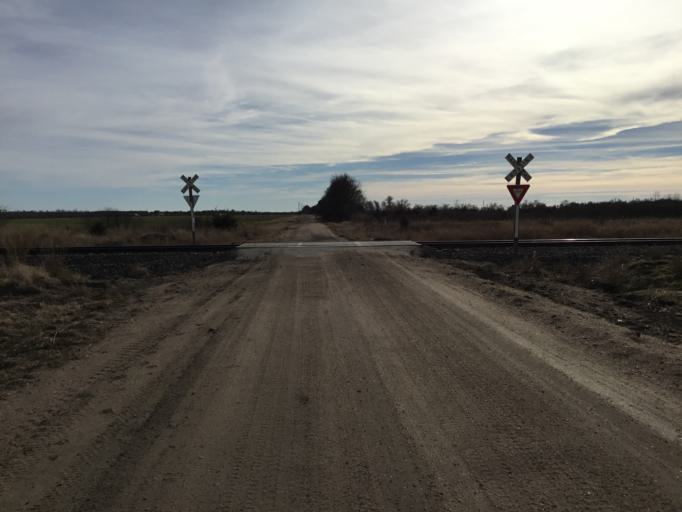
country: US
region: Kansas
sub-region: McPherson County
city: McPherson
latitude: 38.3846
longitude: -97.5931
